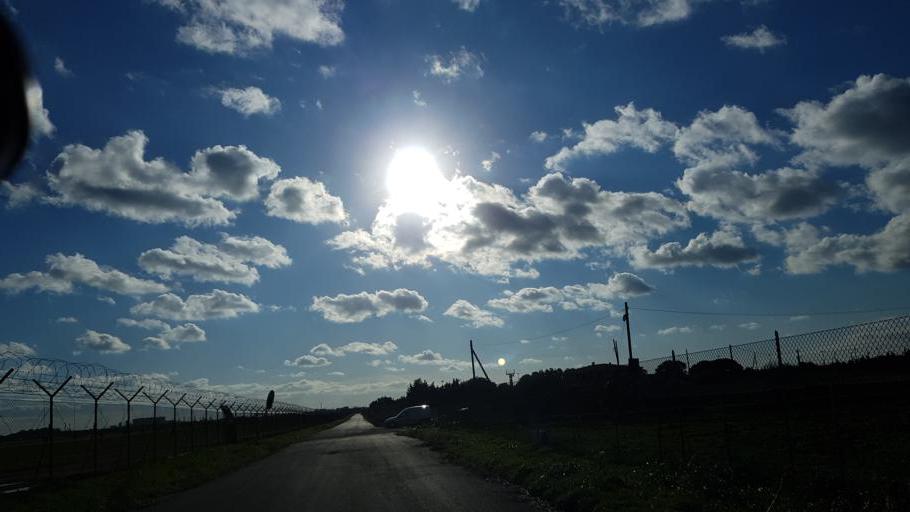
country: IT
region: Apulia
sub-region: Provincia di Brindisi
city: Materdomini
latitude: 40.6647
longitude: 17.9362
